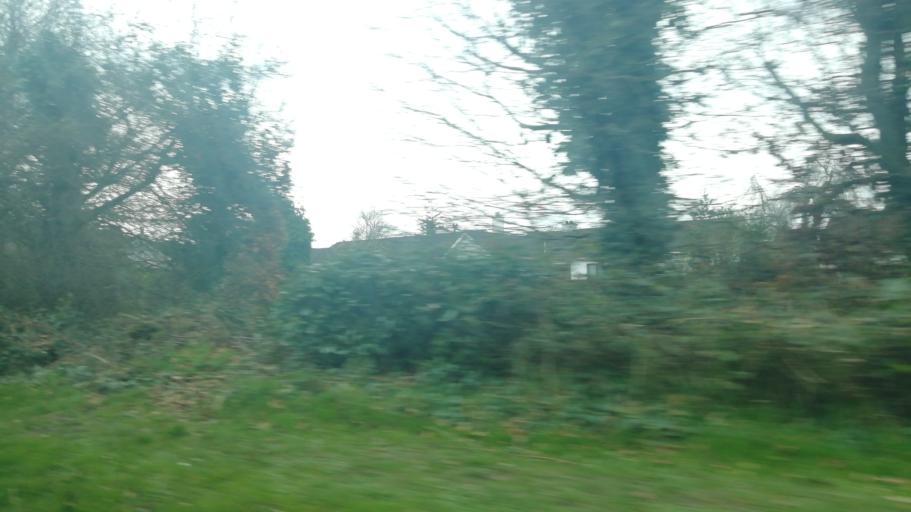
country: IE
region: Leinster
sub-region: Kildare
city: Clane
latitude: 53.2989
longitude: -6.6978
